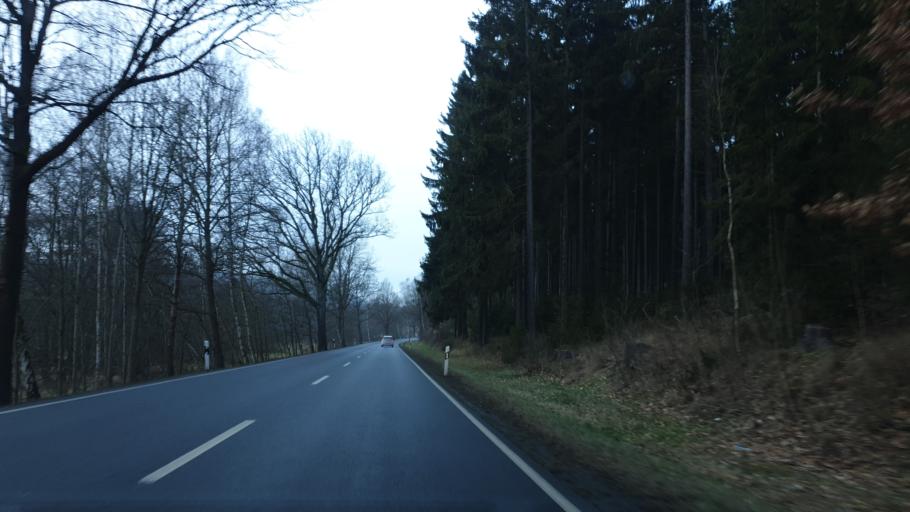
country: DE
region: Saxony
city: Adorf
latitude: 50.2789
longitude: 12.2851
